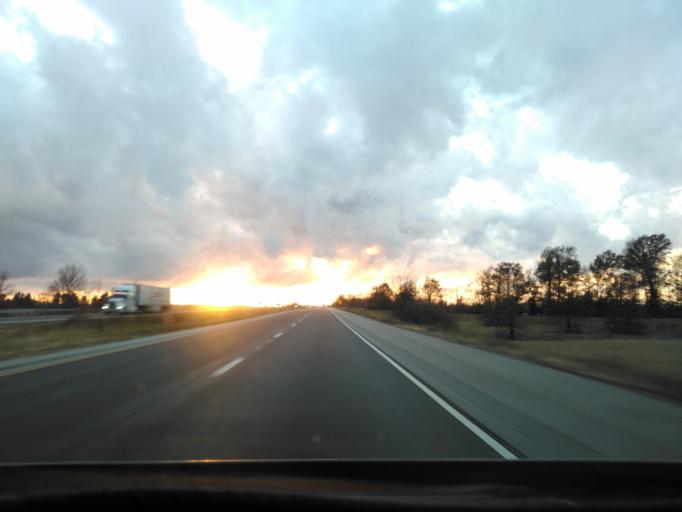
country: US
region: Illinois
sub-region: Fayette County
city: Saint Elmo
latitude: 39.0115
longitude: -88.8575
